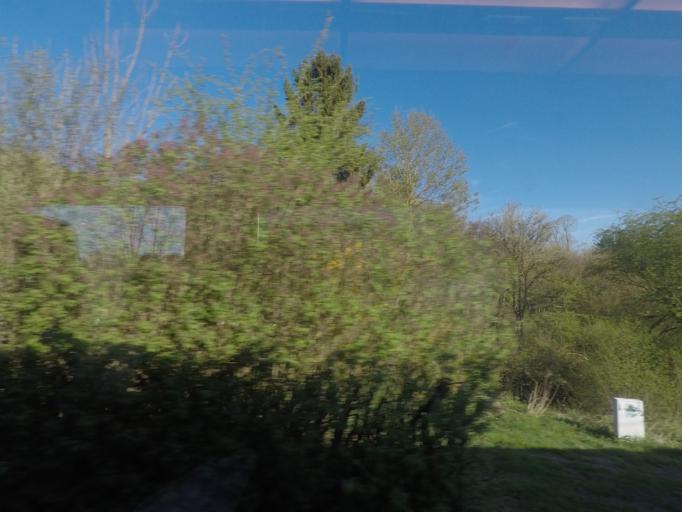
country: BE
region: Wallonia
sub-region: Province de Namur
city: Rochefort
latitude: 50.1753
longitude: 5.2854
